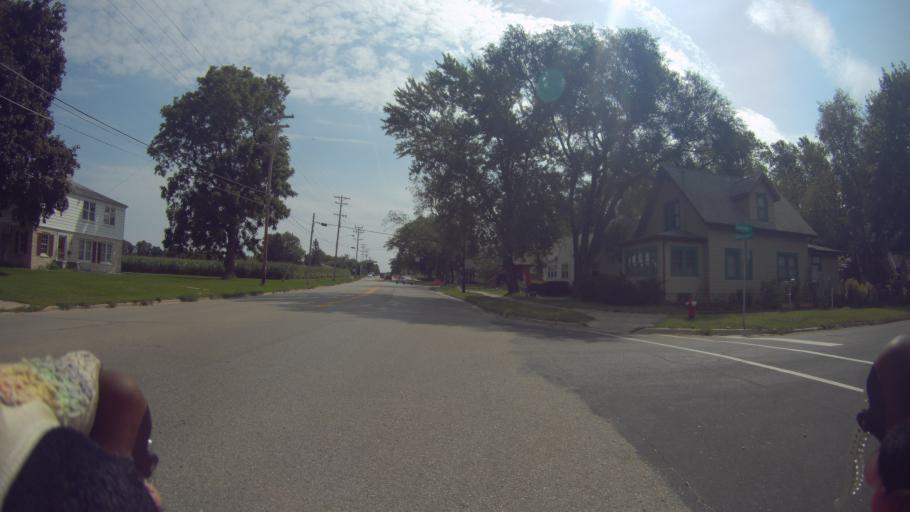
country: US
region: Wisconsin
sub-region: Dane County
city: Monona
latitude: 43.0981
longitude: -89.3286
